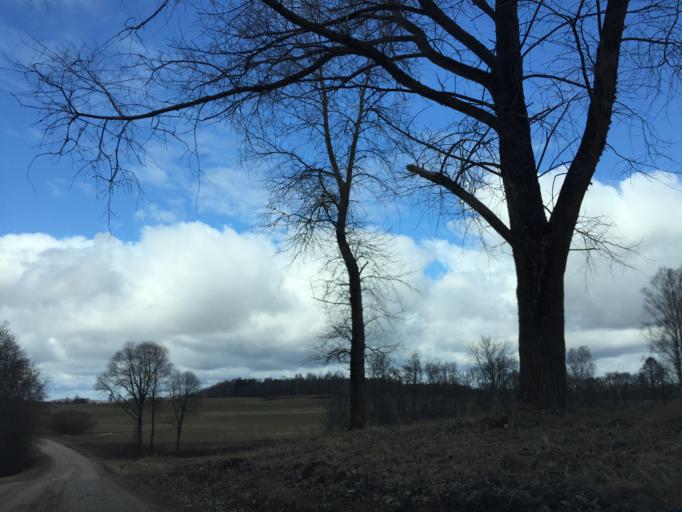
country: LV
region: Akniste
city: Akniste
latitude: 56.0916
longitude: 26.0075
